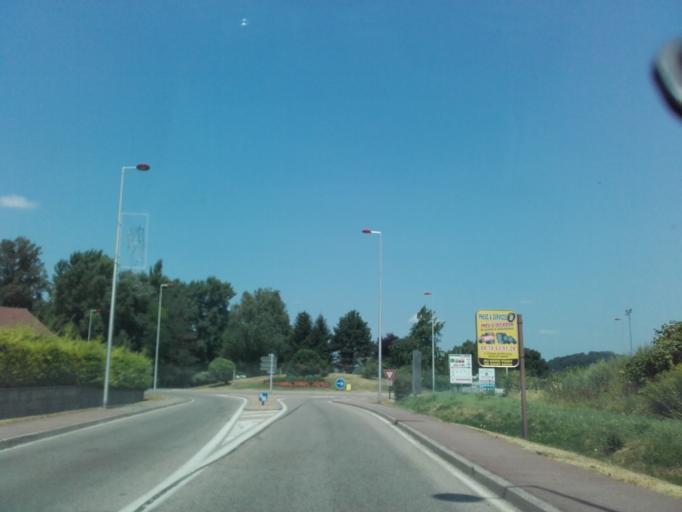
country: FR
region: Rhone-Alpes
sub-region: Departement de l'Isere
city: Nivolas-Vermelle
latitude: 45.5617
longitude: 5.3039
